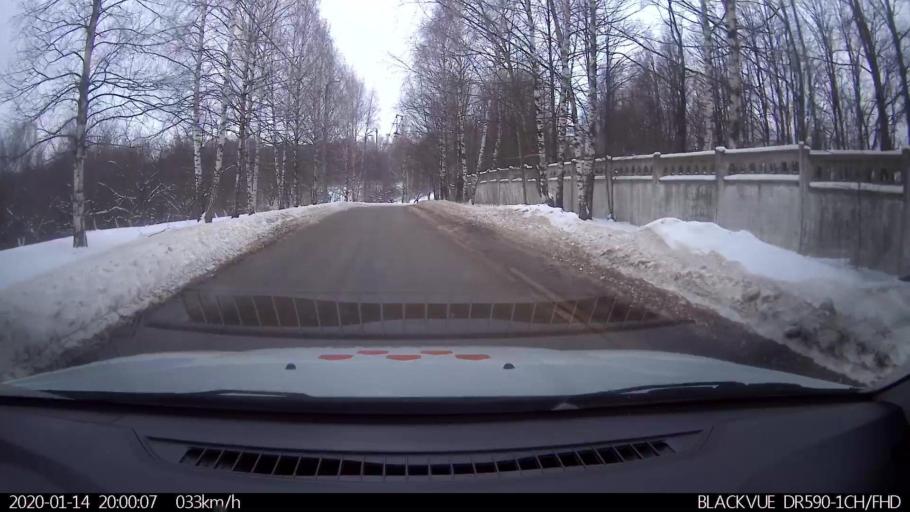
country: RU
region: Nizjnij Novgorod
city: Nizhniy Novgorod
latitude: 56.2398
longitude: 43.9429
